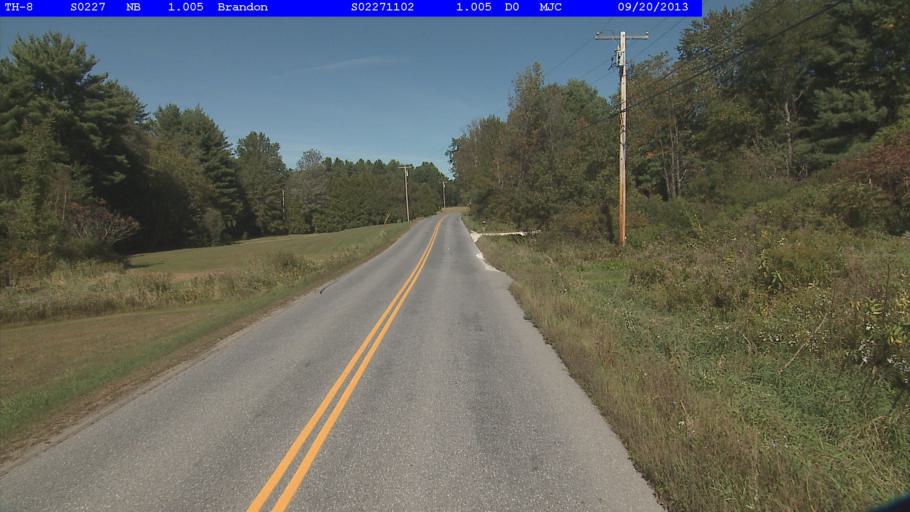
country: US
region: Vermont
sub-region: Rutland County
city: Brandon
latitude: 43.7889
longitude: -73.0538
